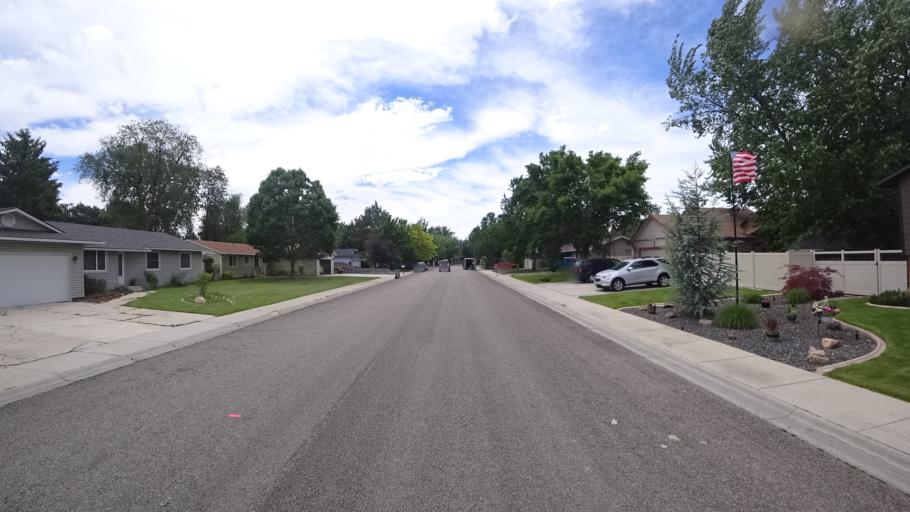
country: US
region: Idaho
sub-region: Ada County
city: Eagle
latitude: 43.6361
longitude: -116.3244
